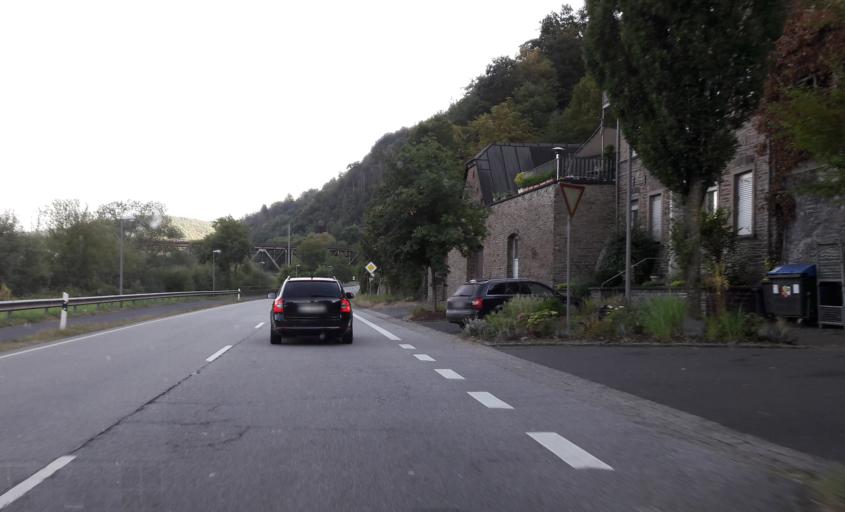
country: DE
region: Rheinland-Pfalz
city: Alf
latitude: 50.0507
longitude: 7.1293
